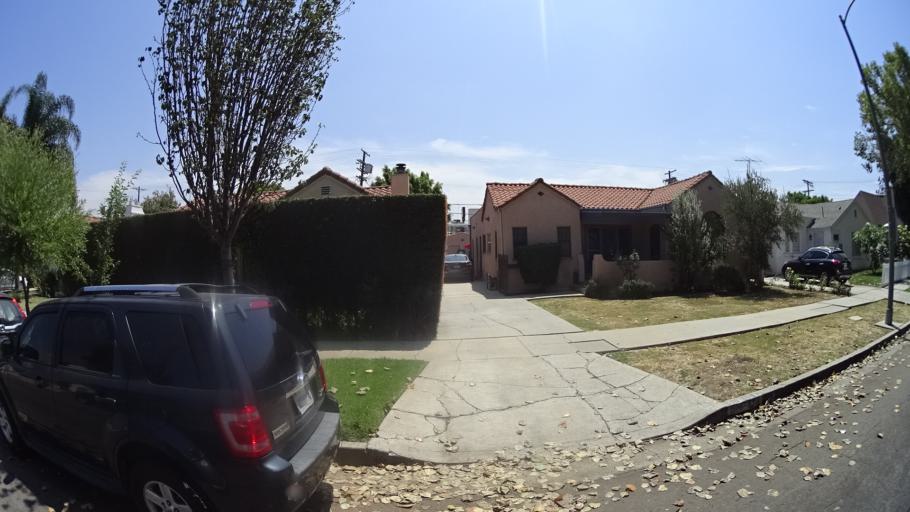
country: US
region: California
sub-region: Los Angeles County
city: West Hollywood
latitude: 34.0824
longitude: -118.3452
